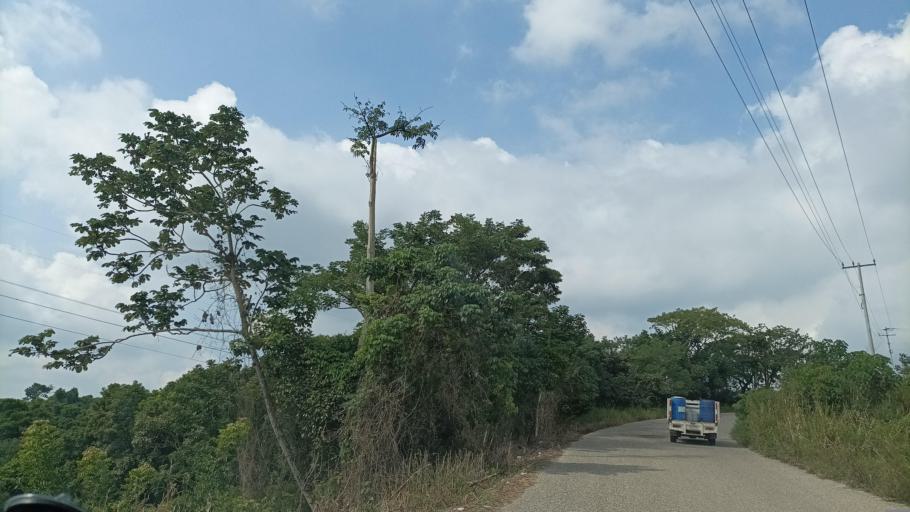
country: MX
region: Veracruz
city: Las Choapas
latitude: 17.7992
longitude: -94.1105
